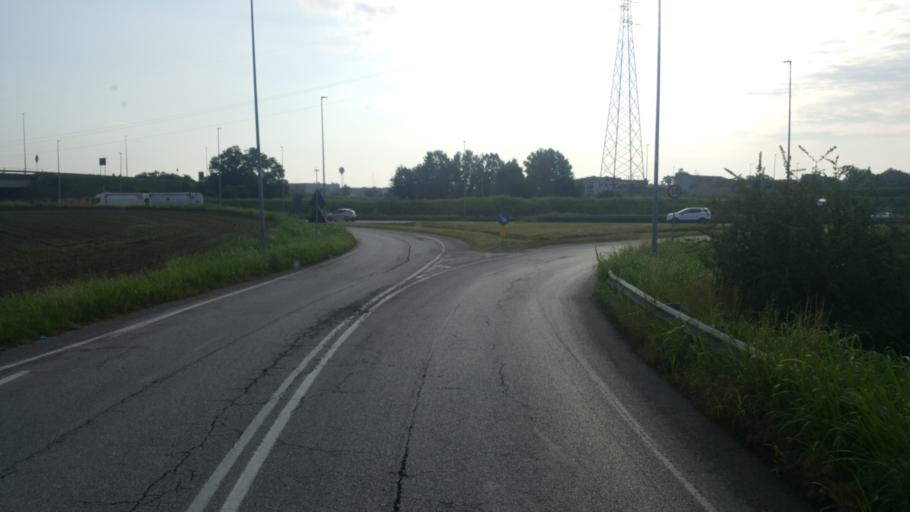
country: IT
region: Lombardy
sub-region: Provincia di Brescia
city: Manerbio
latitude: 45.3593
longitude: 10.1542
